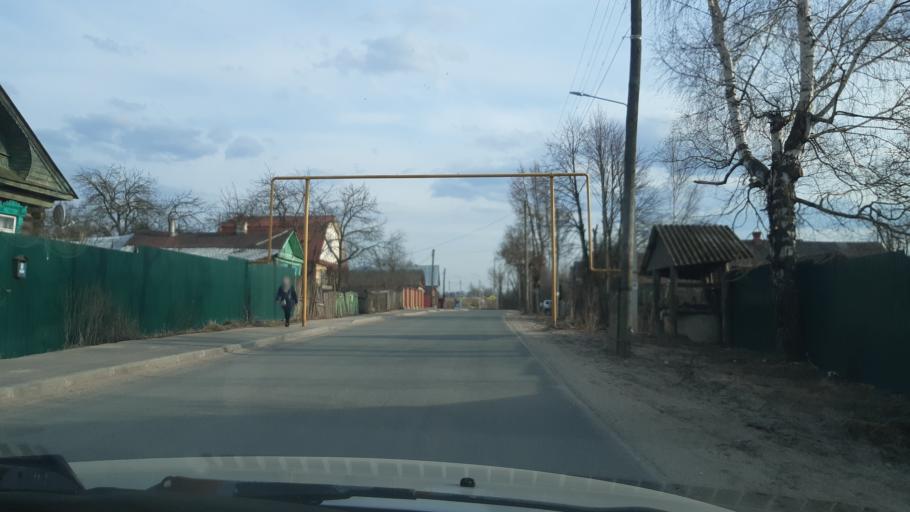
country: RU
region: Vladimir
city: Nikologory
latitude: 56.1367
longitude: 41.9917
